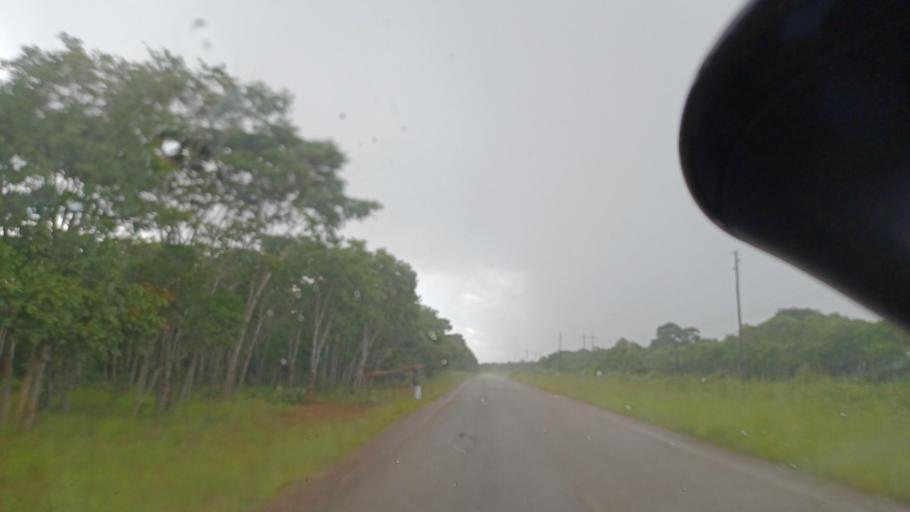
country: ZM
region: North-Western
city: Kasempa
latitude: -13.0915
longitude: 25.9326
